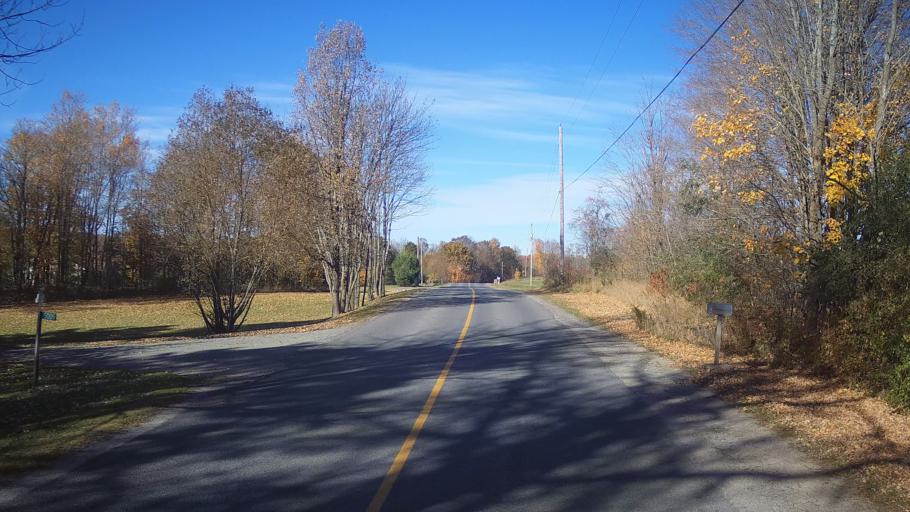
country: CA
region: Ontario
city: Kingston
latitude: 44.4393
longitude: -76.5231
